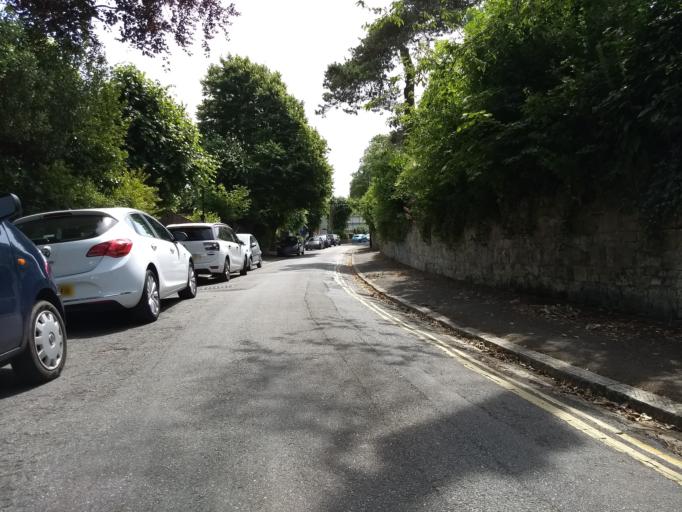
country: GB
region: England
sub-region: Isle of Wight
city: Shanklin
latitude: 50.6241
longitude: -1.1769
